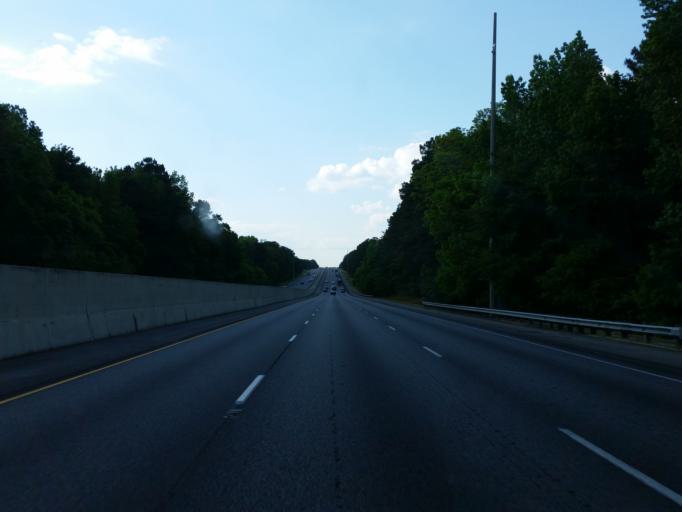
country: US
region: Georgia
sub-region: Bibb County
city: West Point
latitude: 32.9202
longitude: -83.7992
